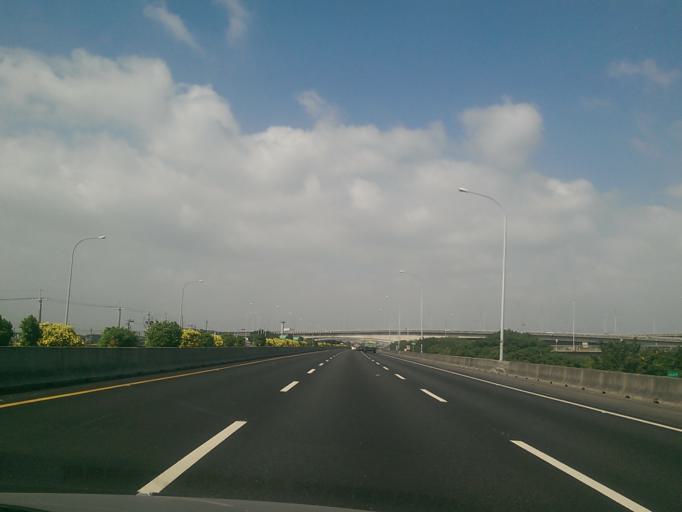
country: TW
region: Taiwan
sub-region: Changhua
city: Chang-hua
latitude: 23.9792
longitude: 120.5066
